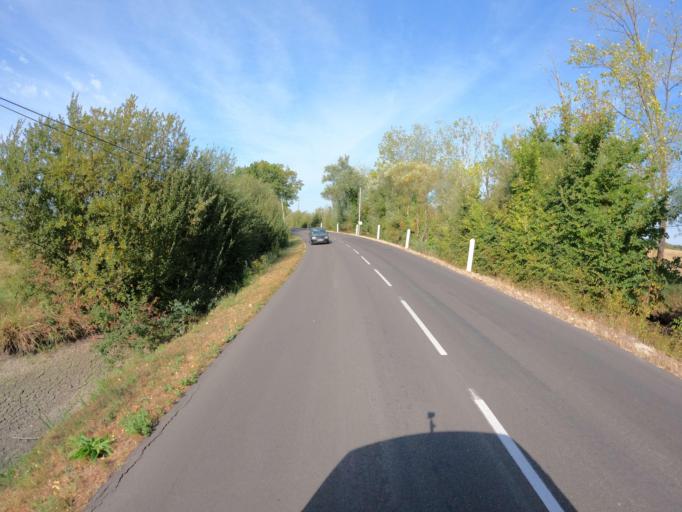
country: FR
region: Pays de la Loire
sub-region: Departement de la Vendee
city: Soullans
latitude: 46.8076
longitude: -1.9357
